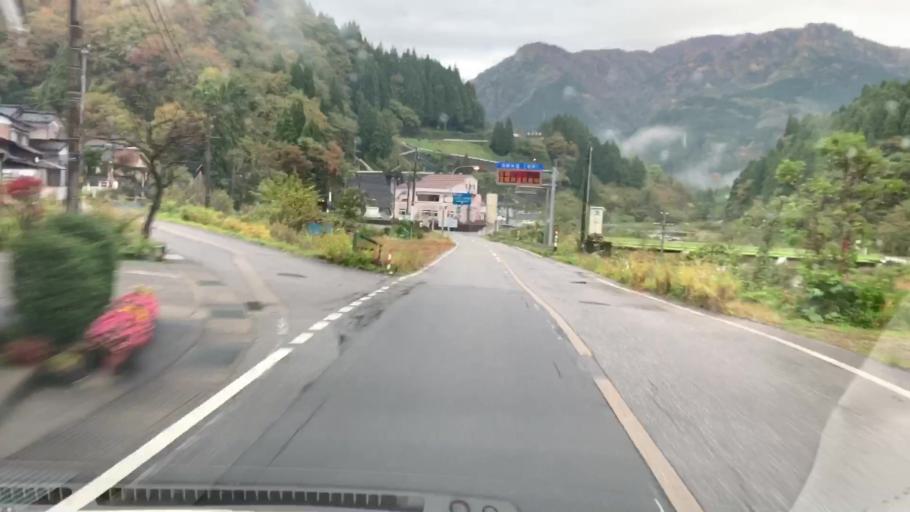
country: JP
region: Toyama
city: Kamiichi
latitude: 36.5720
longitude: 137.3806
